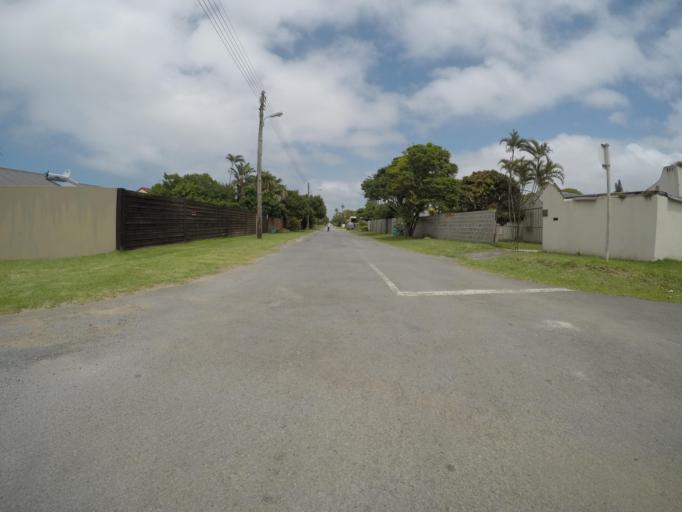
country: ZA
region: Eastern Cape
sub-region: Buffalo City Metropolitan Municipality
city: East London
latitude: -32.9420
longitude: 28.0123
